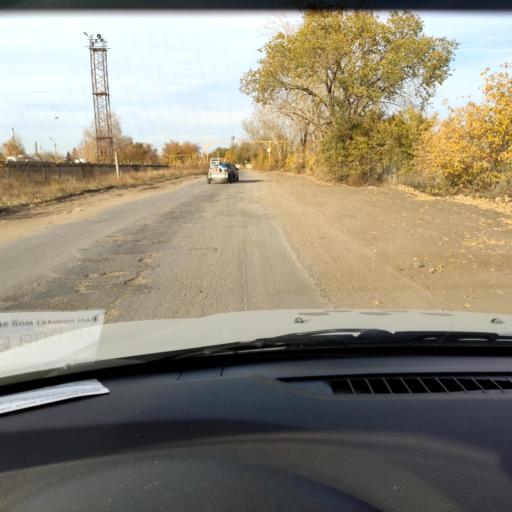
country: RU
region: Samara
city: Zhigulevsk
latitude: 53.4723
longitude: 49.5010
